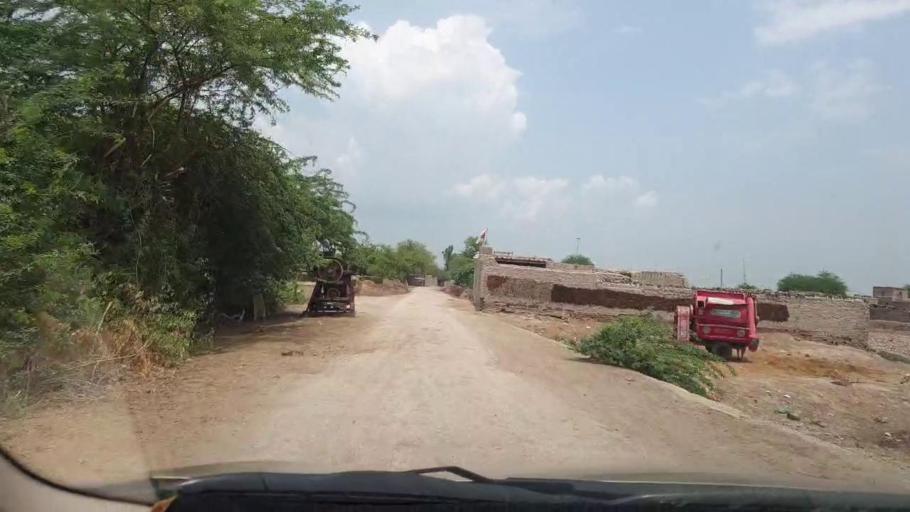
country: PK
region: Sindh
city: Larkana
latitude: 27.5634
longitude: 68.1251
